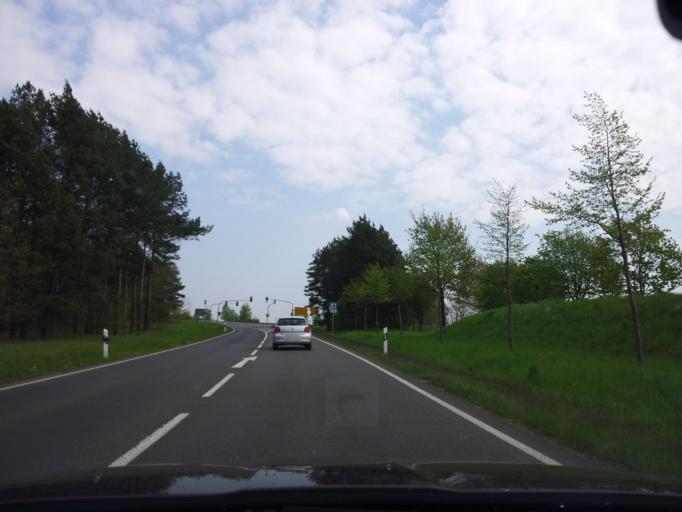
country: DE
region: Brandenburg
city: Seelow
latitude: 52.5187
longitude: 14.3472
